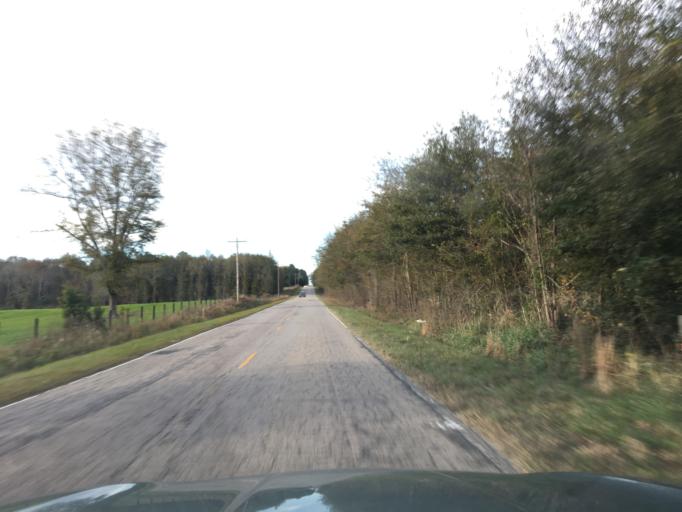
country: US
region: South Carolina
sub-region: Lexington County
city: Red Bank
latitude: 33.7363
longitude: -81.3613
